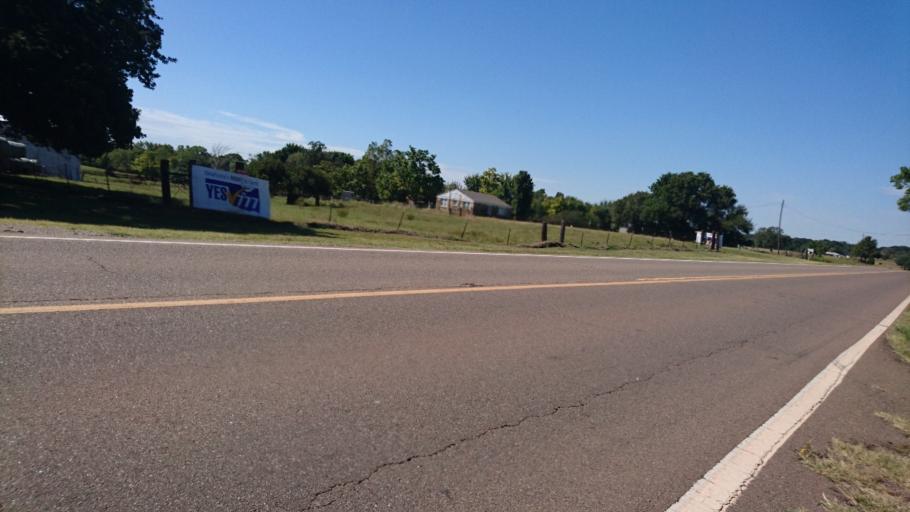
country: US
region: Oklahoma
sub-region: Oklahoma County
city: Luther
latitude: 35.6671
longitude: -97.2377
